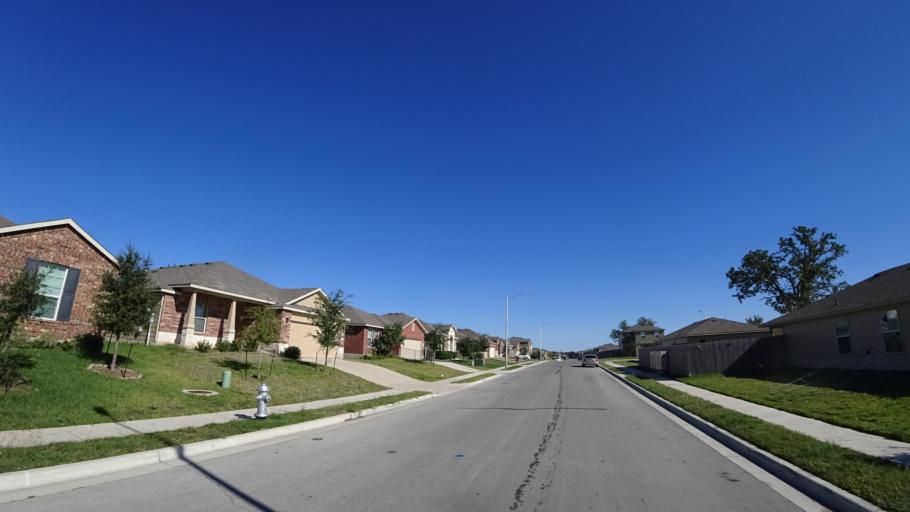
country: US
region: Texas
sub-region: Travis County
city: Hornsby Bend
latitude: 30.2797
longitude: -97.6262
